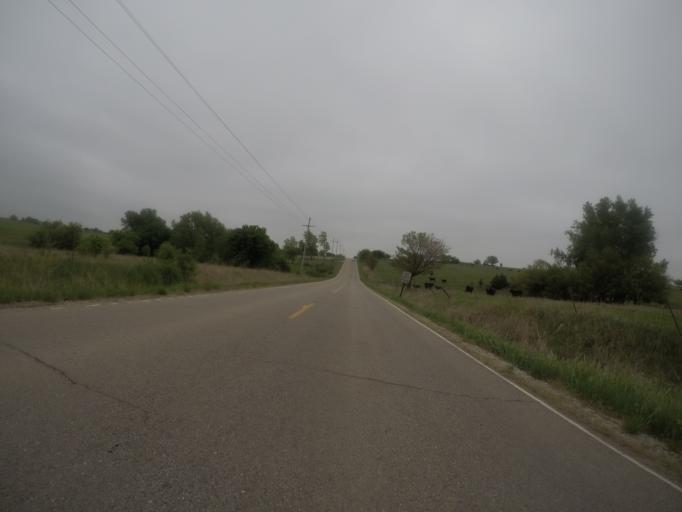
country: US
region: Kansas
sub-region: Pottawatomie County
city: Westmoreland
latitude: 39.5222
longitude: -96.3020
